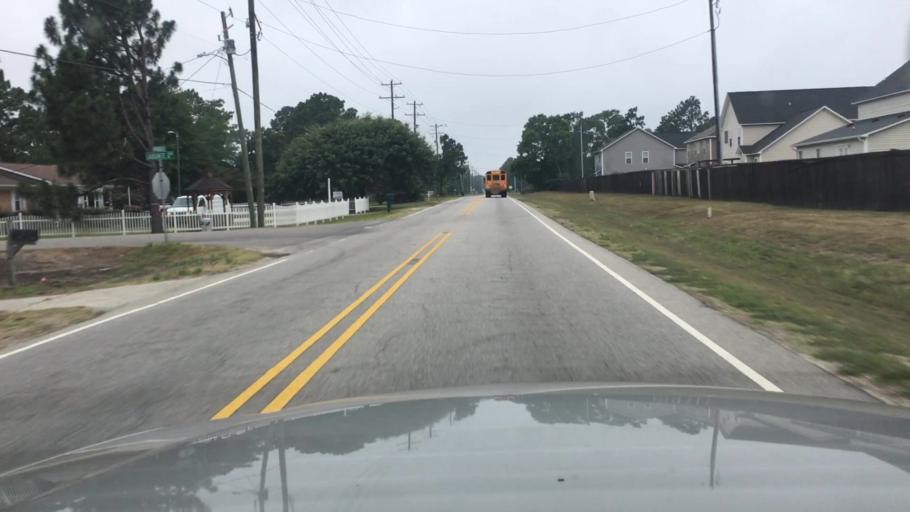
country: US
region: North Carolina
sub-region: Cumberland County
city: Hope Mills
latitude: 34.9759
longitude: -78.9756
